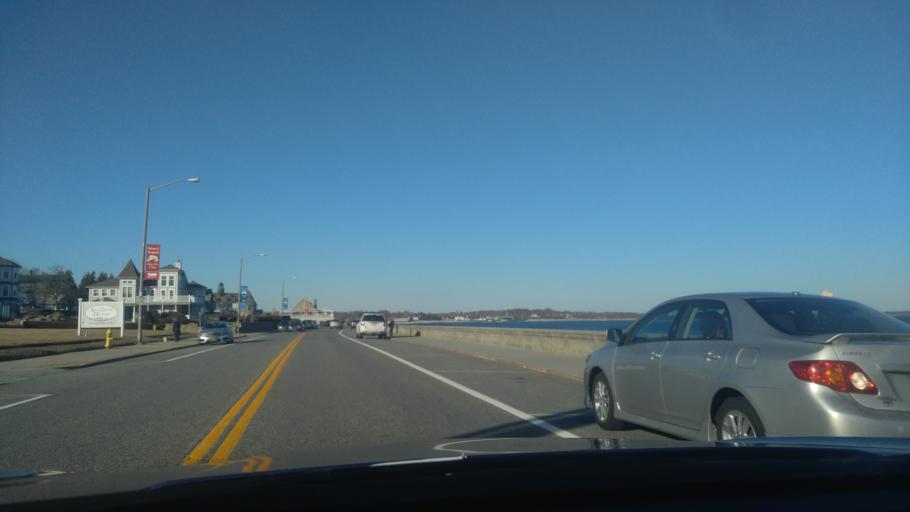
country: US
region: Rhode Island
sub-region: Washington County
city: Narragansett Pier
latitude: 41.4275
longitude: -71.4559
